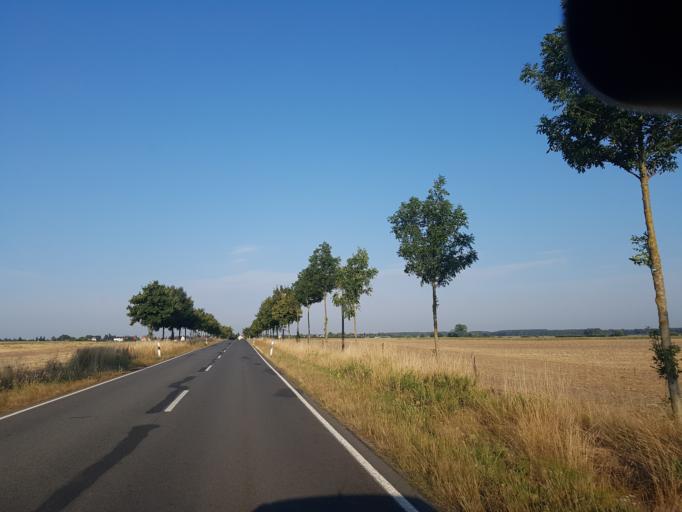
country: DE
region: Brandenburg
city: Plessa
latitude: 51.5352
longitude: 13.6482
